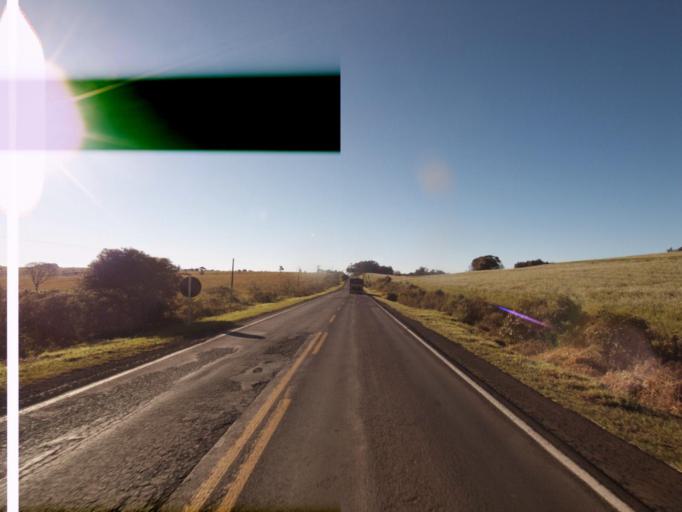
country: AR
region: Misiones
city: Bernardo de Irigoyen
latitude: -26.2965
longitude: -53.5541
